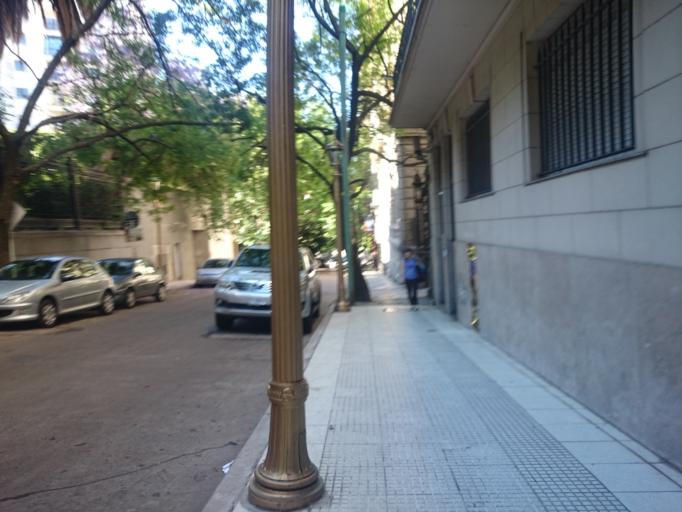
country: AR
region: Buenos Aires F.D.
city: Retiro
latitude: -34.5938
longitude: -58.3778
